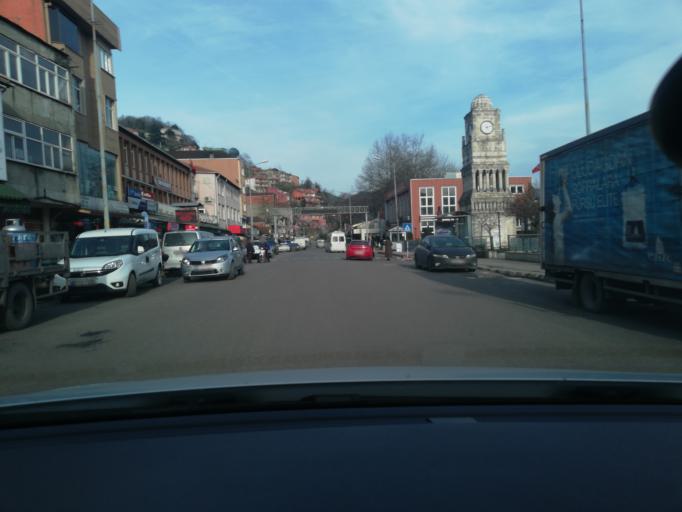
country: TR
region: Zonguldak
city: Kilimli
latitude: 41.4994
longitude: 31.8725
